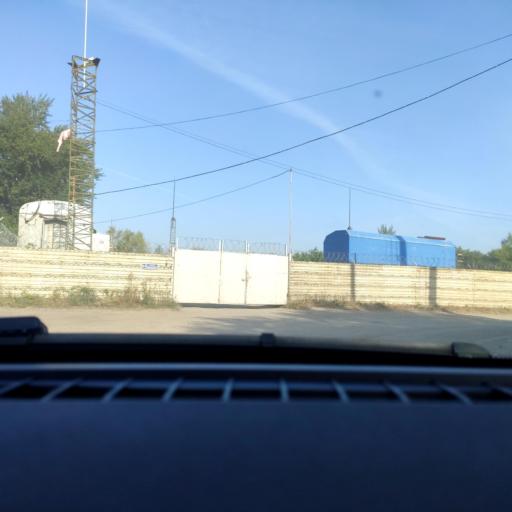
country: RU
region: Voronezj
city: Voronezh
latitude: 51.6457
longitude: 39.2761
